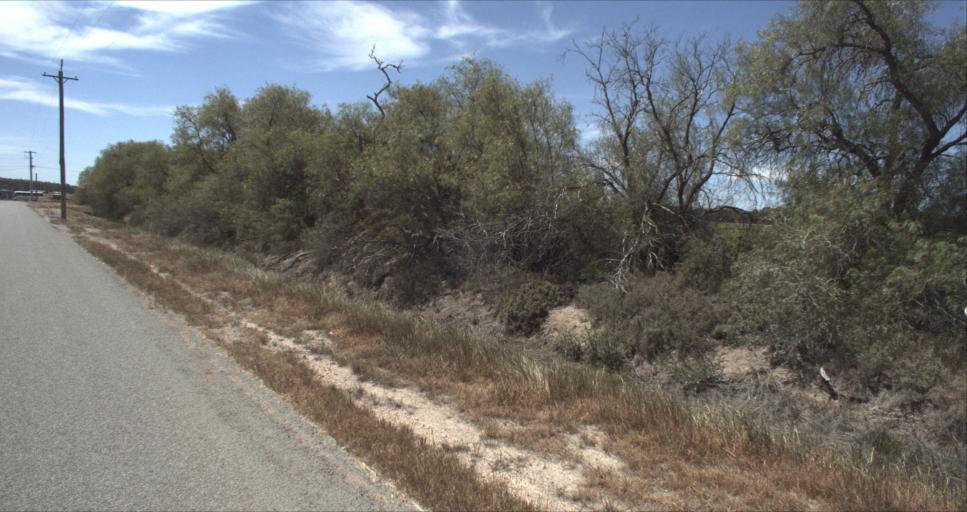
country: AU
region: New South Wales
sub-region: Leeton
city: Leeton
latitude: -34.5944
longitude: 146.4168
